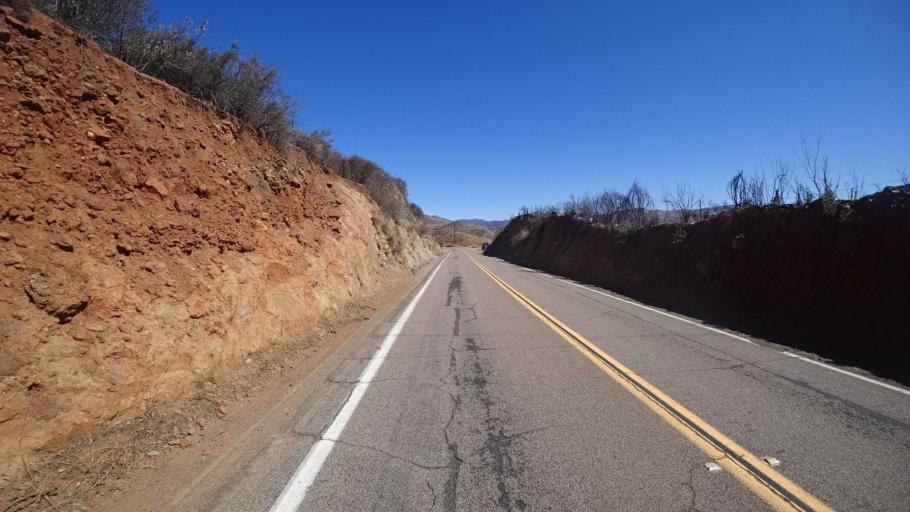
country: US
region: California
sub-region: San Diego County
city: Alpine
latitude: 32.7127
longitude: -116.7064
